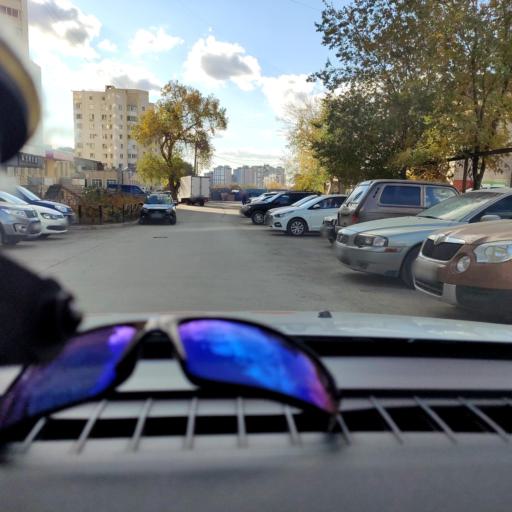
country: RU
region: Samara
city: Samara
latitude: 53.1978
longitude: 50.1518
